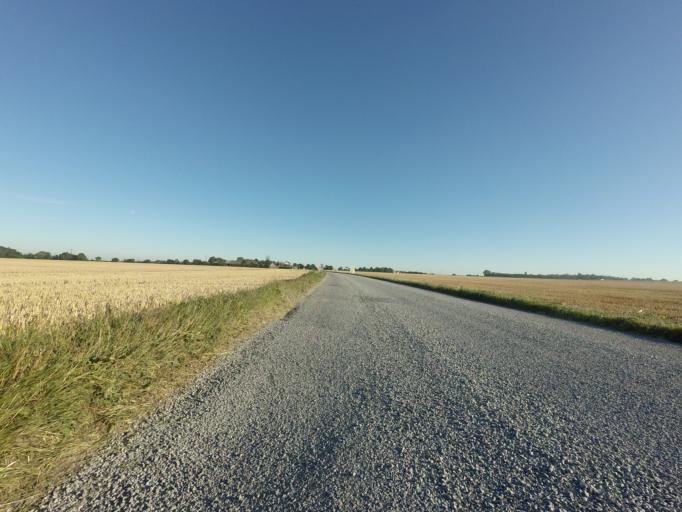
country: GB
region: England
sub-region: Kent
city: Herne Bay
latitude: 51.3397
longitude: 1.1898
